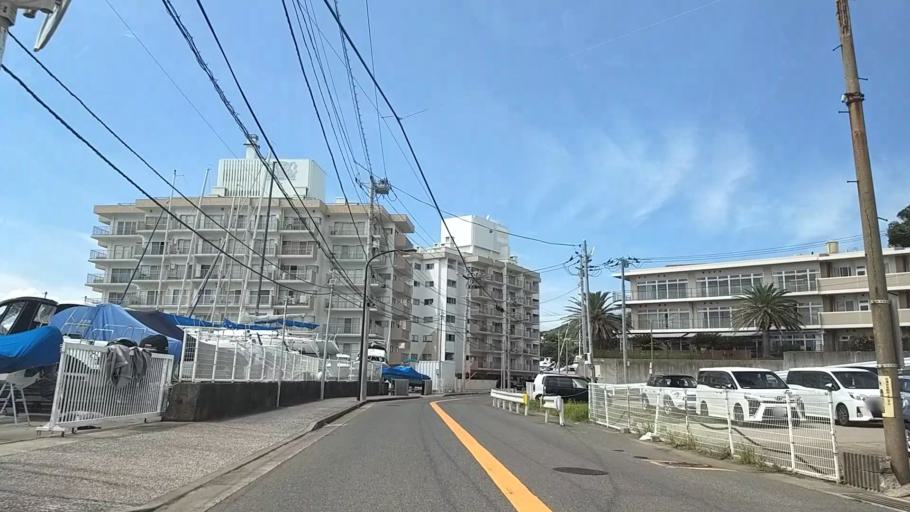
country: JP
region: Kanagawa
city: Hayama
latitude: 35.2283
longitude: 139.6036
